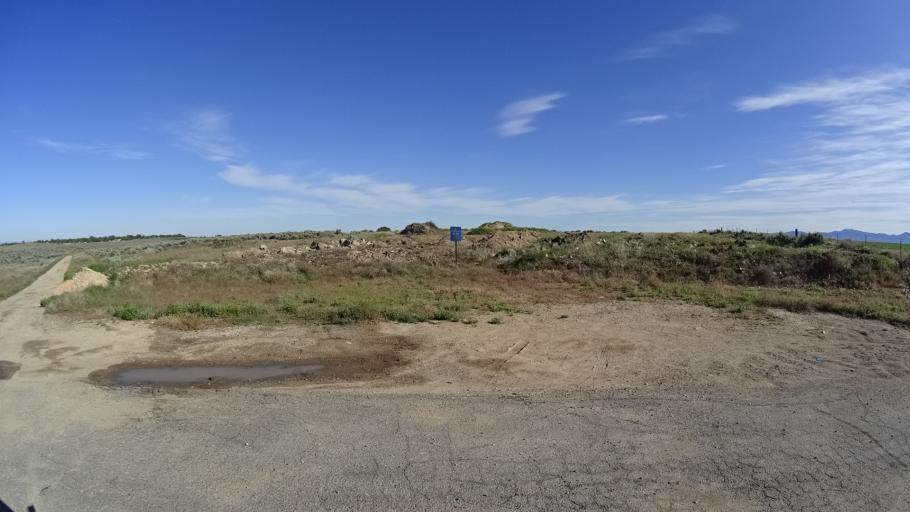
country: US
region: Idaho
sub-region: Ada County
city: Garden City
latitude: 43.5248
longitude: -116.2895
